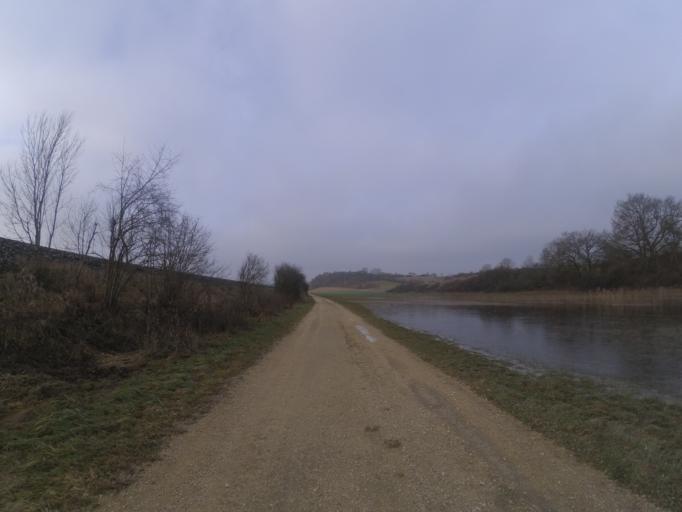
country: DE
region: Baden-Wuerttemberg
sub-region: Tuebingen Region
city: Untermarchtal
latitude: 48.2432
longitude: 9.5993
